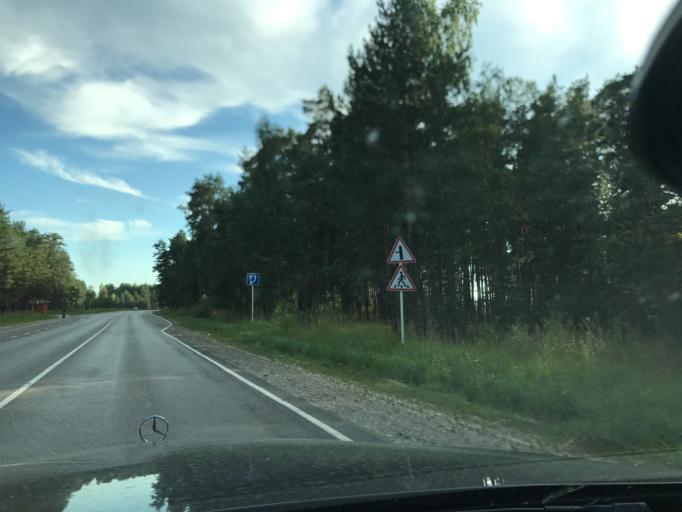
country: RU
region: Vladimir
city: Kommunar
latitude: 56.0414
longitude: 40.4310
